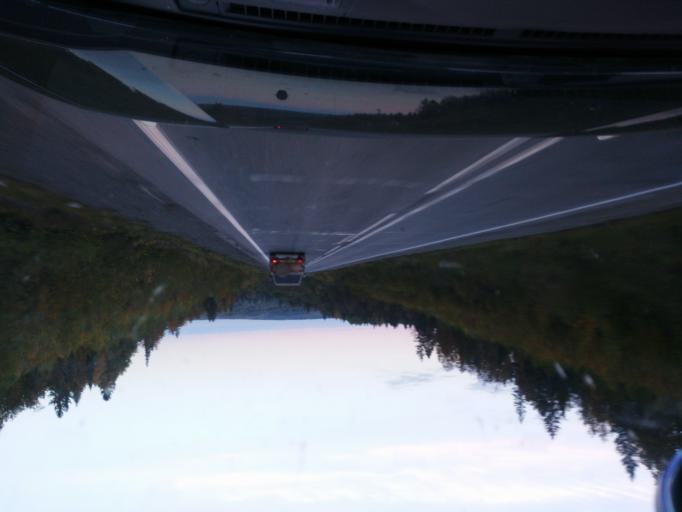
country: RU
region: Perm
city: Sylva
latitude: 58.2938
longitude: 56.7538
